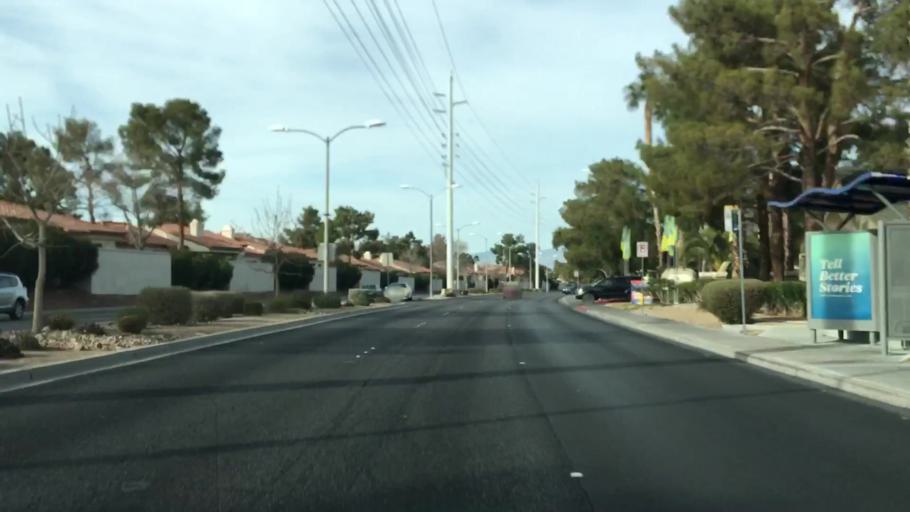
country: US
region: Nevada
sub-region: Clark County
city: Whitney
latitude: 36.0572
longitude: -115.0844
